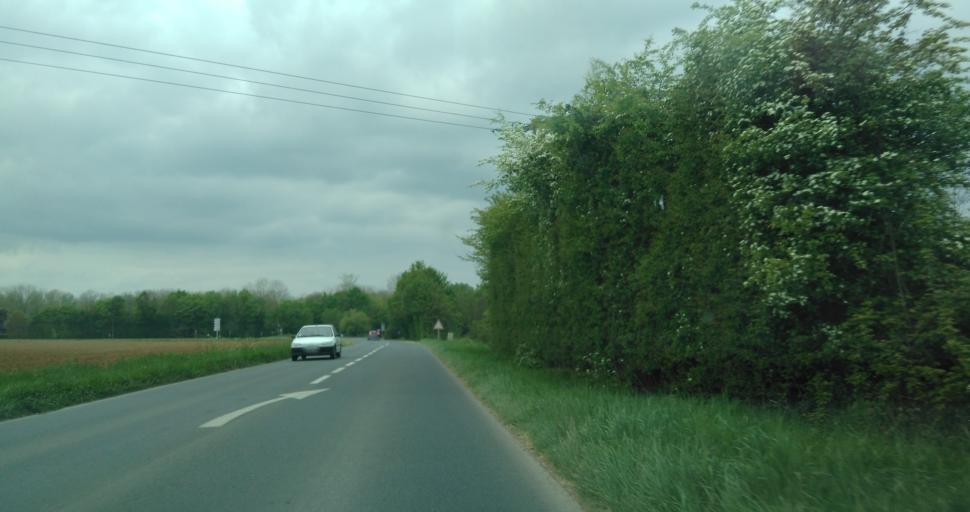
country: FR
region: Poitou-Charentes
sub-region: Departement des Deux-Sevres
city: Coulon
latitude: 46.3189
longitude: -0.5736
